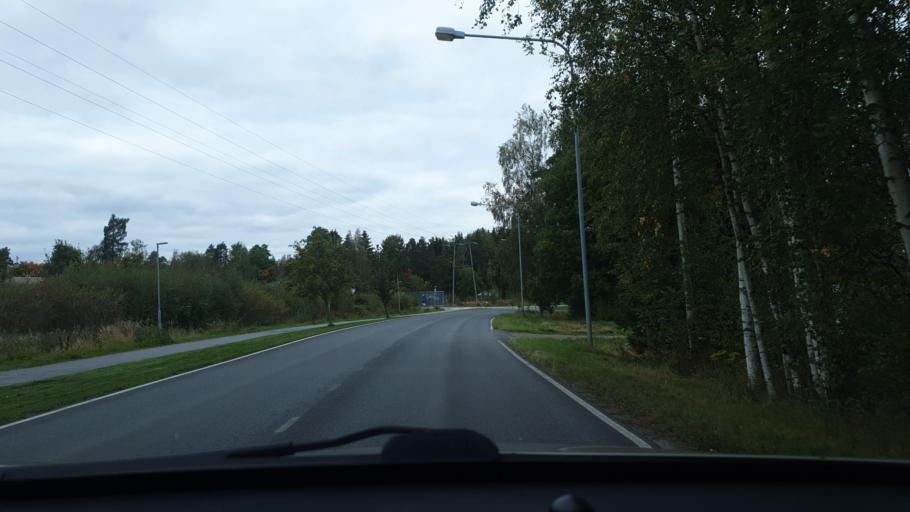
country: FI
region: Ostrobothnia
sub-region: Vaasa
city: Teeriniemi
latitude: 63.0934
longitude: 21.6979
